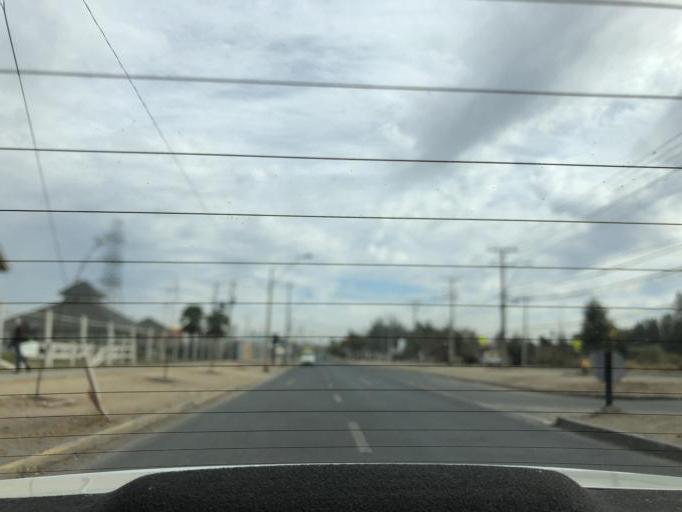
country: CL
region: Santiago Metropolitan
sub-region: Provincia de Cordillera
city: Puente Alto
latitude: -33.6114
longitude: -70.5444
